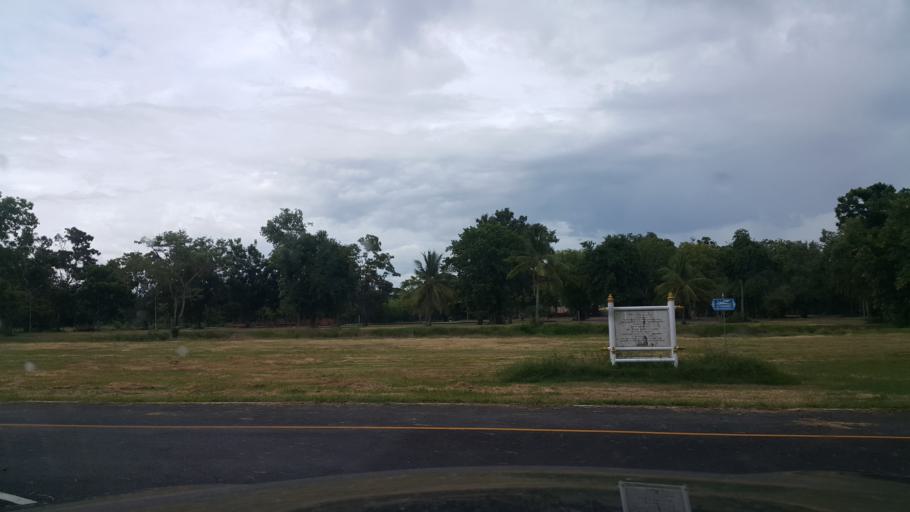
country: TH
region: Sukhothai
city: Ban Na
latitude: 17.0294
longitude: 99.6968
